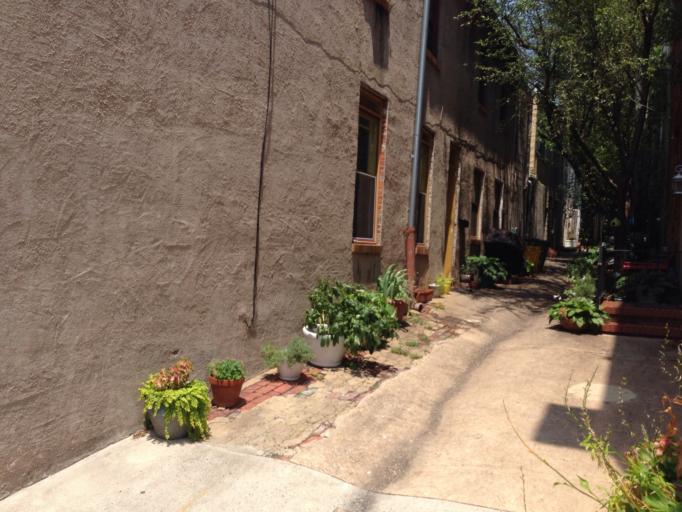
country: US
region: Maryland
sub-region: City of Baltimore
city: Baltimore
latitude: 39.2850
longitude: -76.5845
